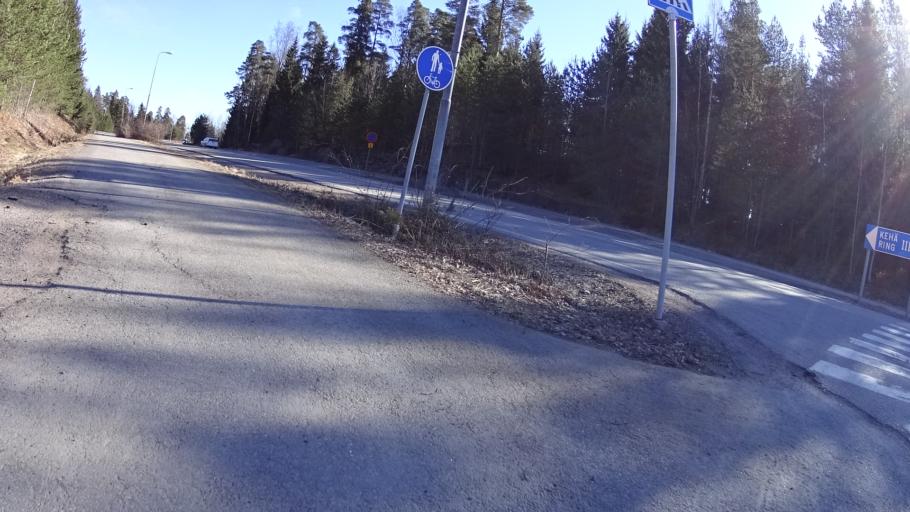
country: FI
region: Uusimaa
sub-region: Helsinki
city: Kauniainen
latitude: 60.2397
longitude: 24.6911
